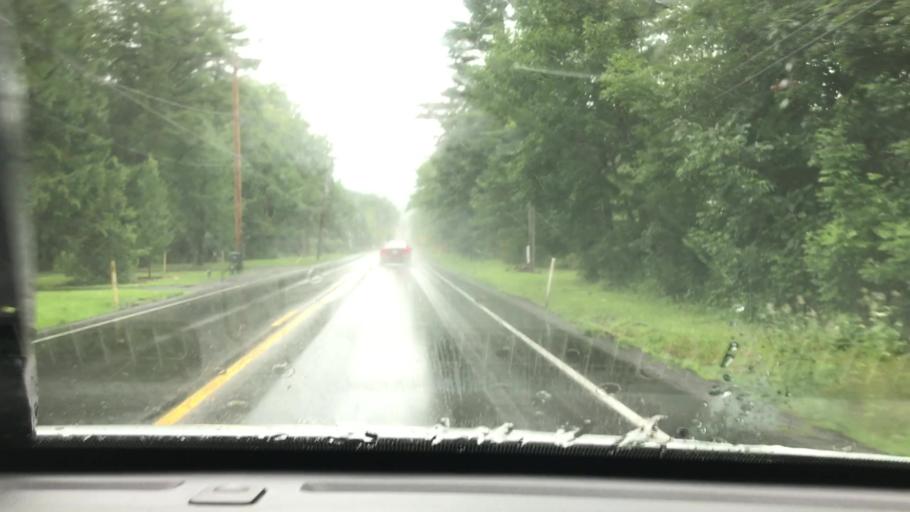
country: US
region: Pennsylvania
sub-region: Blair County
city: Tyrone
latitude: 40.7338
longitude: -78.1929
